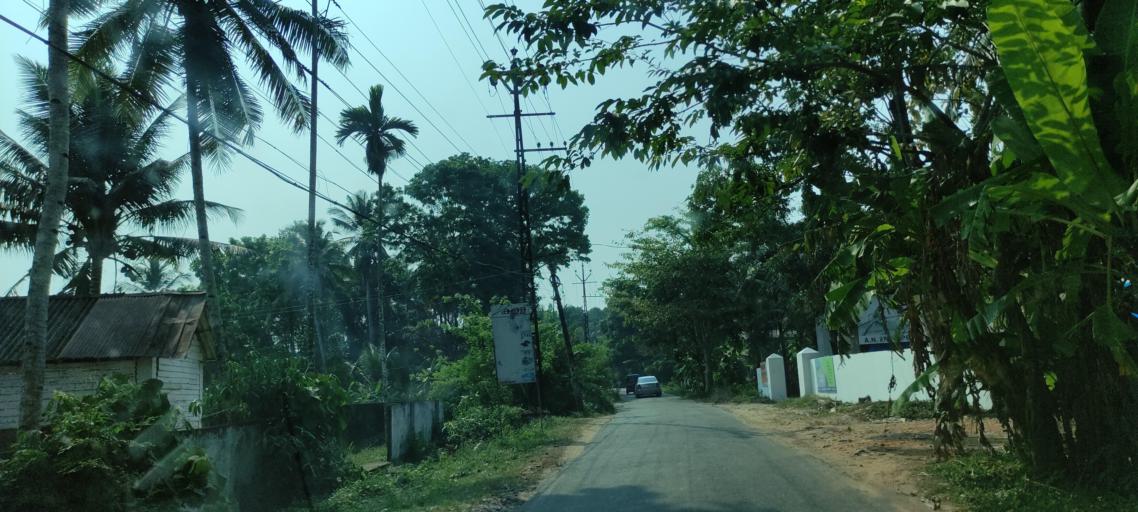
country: IN
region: Kerala
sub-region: Pattanamtitta
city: Tiruvalla
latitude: 9.3553
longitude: 76.5233
